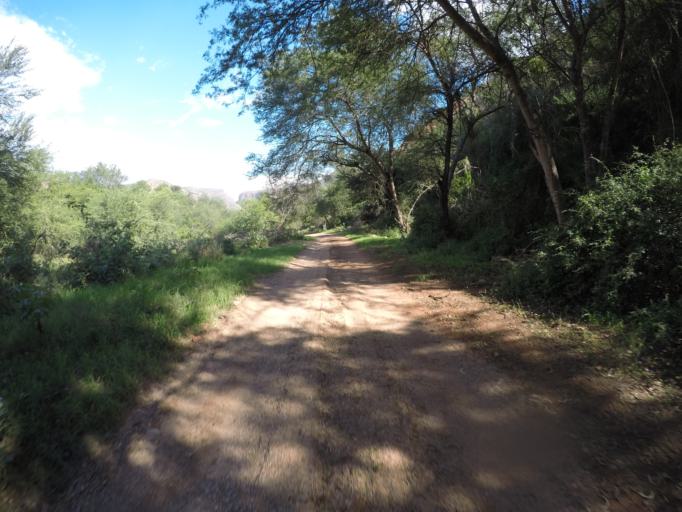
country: ZA
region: Eastern Cape
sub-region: Cacadu District Municipality
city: Kareedouw
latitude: -33.6635
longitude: 24.3898
